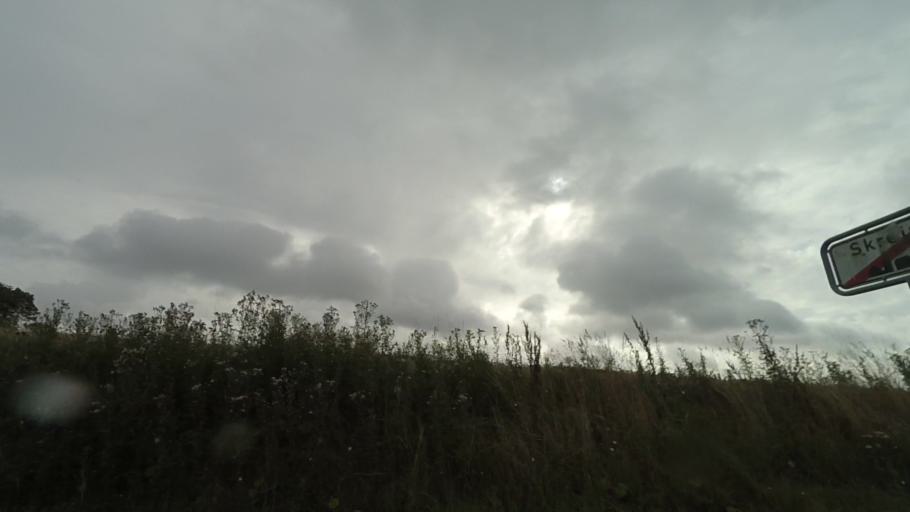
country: DK
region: Central Jutland
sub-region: Syddjurs Kommune
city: Ronde
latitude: 56.3102
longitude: 10.4614
